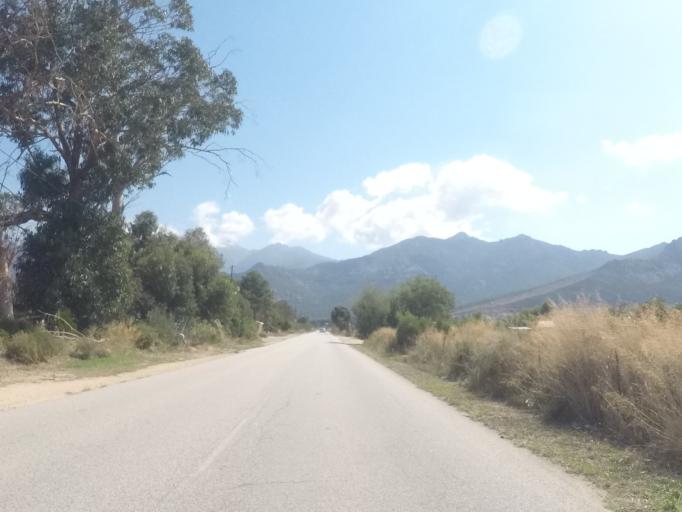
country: FR
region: Corsica
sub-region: Departement de la Haute-Corse
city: Calenzana
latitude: 42.5002
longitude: 8.7928
